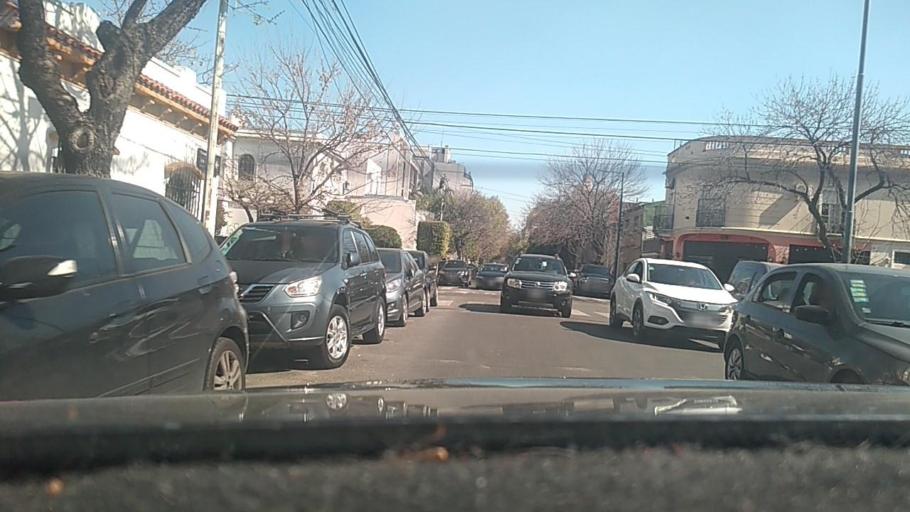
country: AR
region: Buenos Aires F.D.
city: Villa Santa Rita
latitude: -34.6040
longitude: -58.4890
